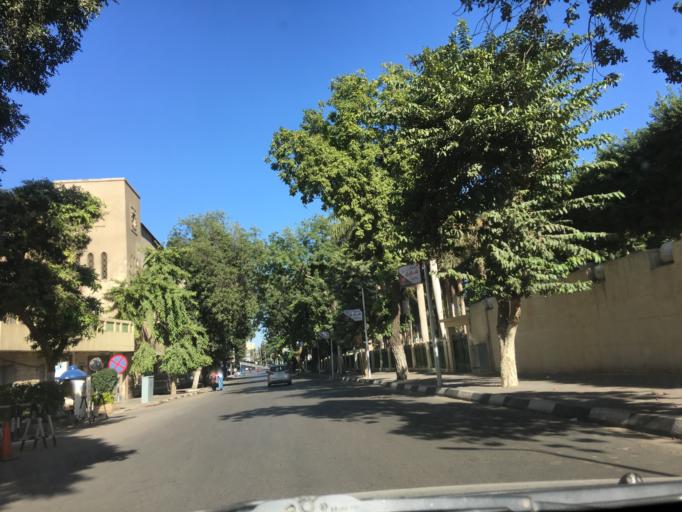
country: EG
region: Muhafazat al Qahirah
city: Cairo
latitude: 30.0445
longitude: 31.2271
